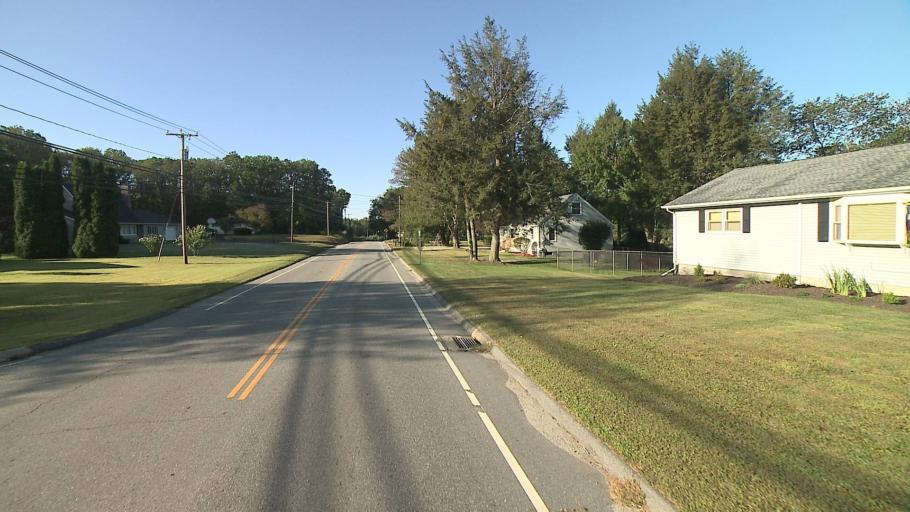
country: US
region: Connecticut
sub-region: Windham County
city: Wauregan
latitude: 41.7692
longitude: -71.8987
